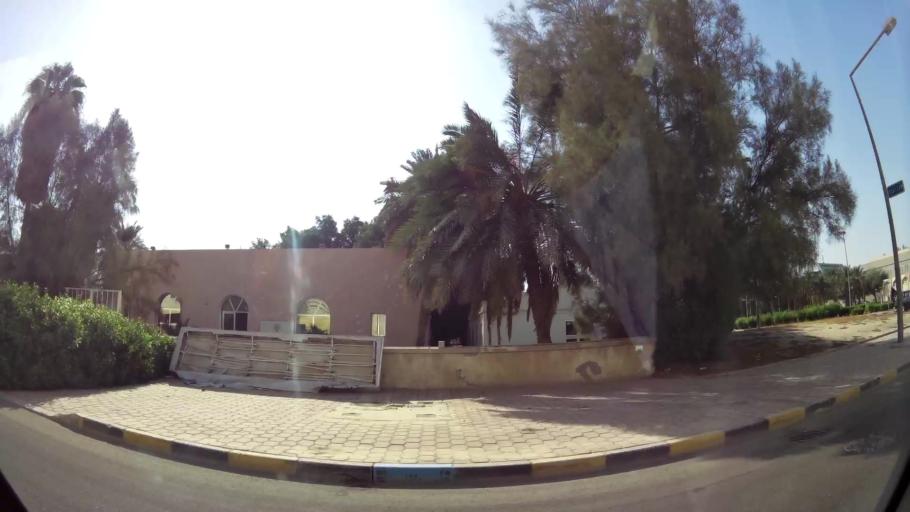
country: KW
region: Al Asimah
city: Ash Shamiyah
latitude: 29.3534
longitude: 47.9446
